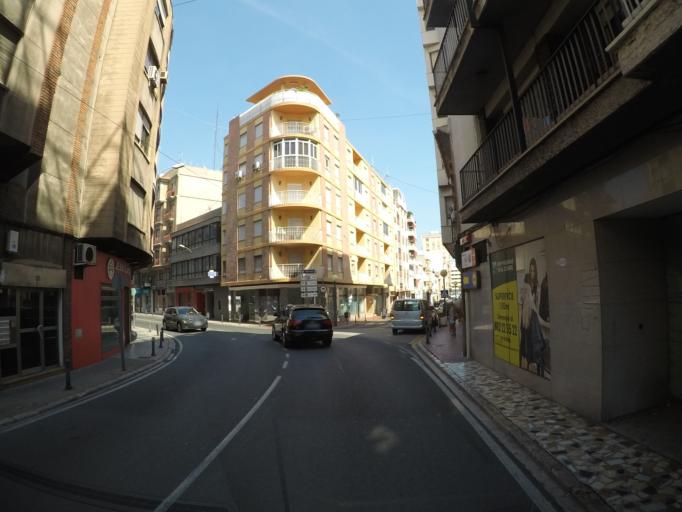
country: ES
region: Valencia
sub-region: Provincia de Valencia
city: Oliva
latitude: 38.9190
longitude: -0.1179
